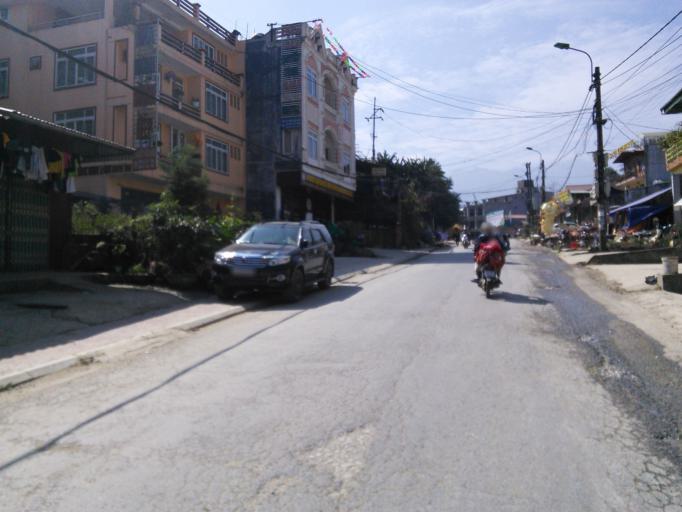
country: VN
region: Lao Cai
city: Sa Pa
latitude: 22.3425
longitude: 103.8565
